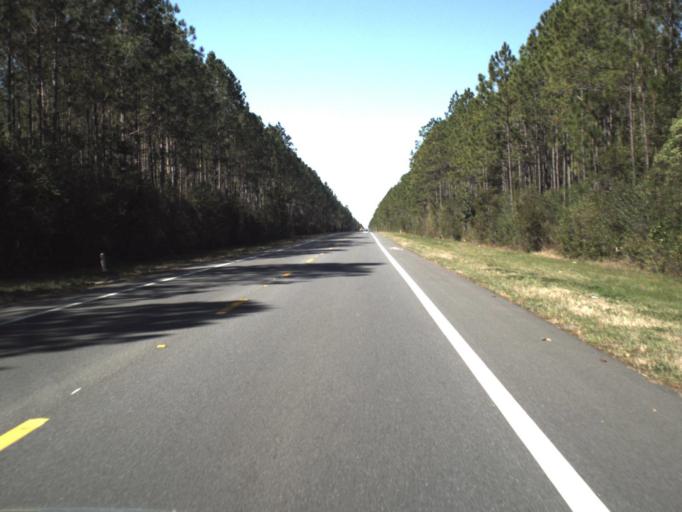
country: US
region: Florida
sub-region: Bay County
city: Callaway
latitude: 30.1527
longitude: -85.5114
